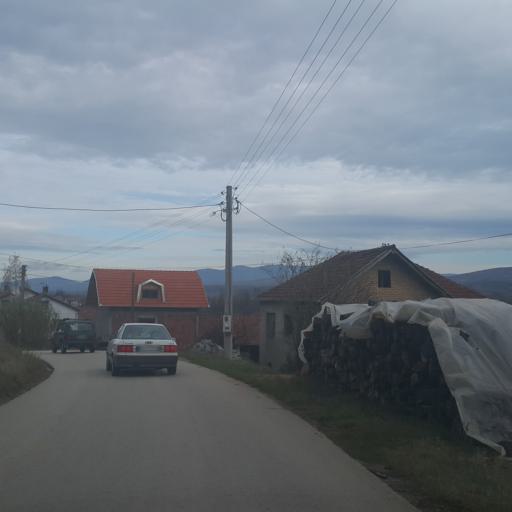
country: RS
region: Central Serbia
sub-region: Zajecarski Okrug
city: Knjazevac
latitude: 43.5897
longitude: 22.2519
